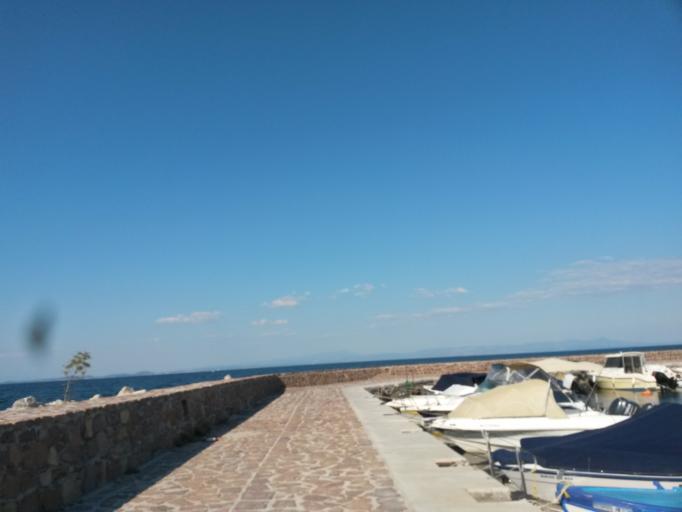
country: GR
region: North Aegean
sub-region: Nomos Lesvou
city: Pamfylla
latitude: 39.1825
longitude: 26.4992
